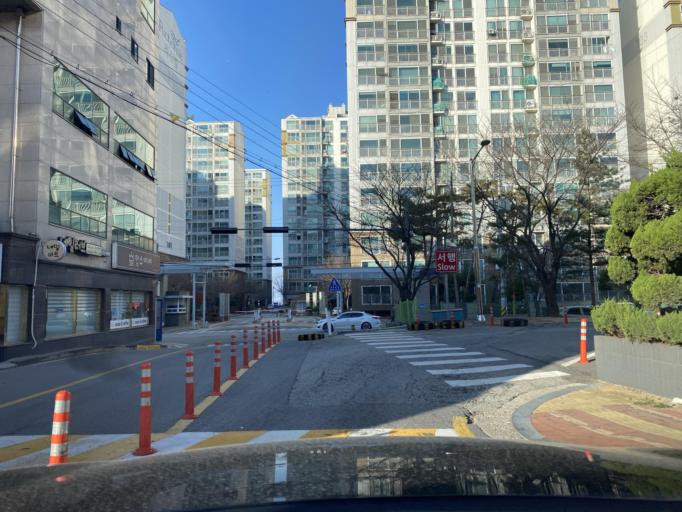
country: KR
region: Chungcheongnam-do
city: Yesan
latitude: 36.6947
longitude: 126.8321
